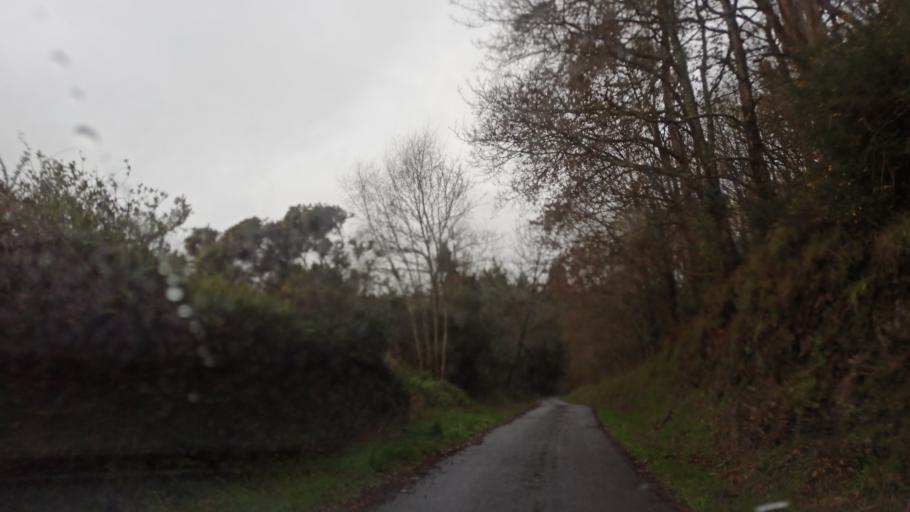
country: ES
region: Galicia
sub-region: Provincia da Coruna
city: Cesuras
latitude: 43.1773
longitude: -8.1579
